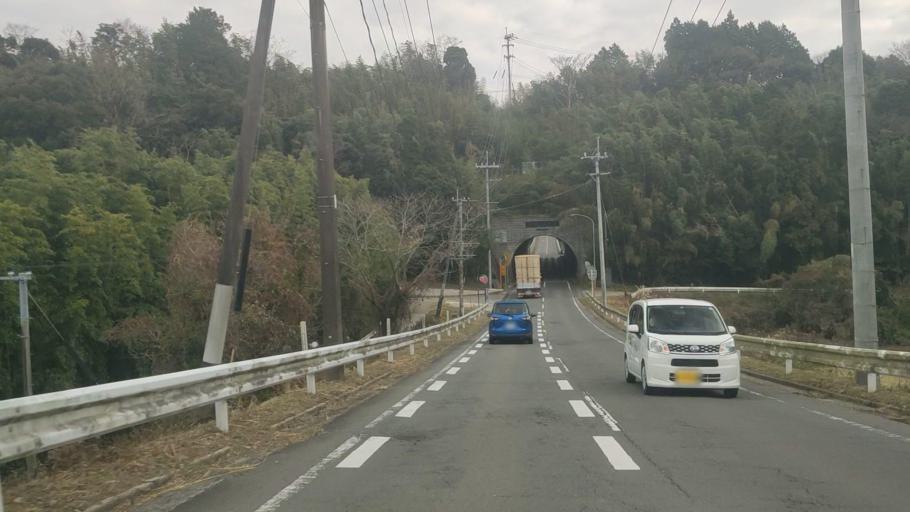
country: JP
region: Nagasaki
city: Shimabara
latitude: 32.8534
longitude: 130.2452
